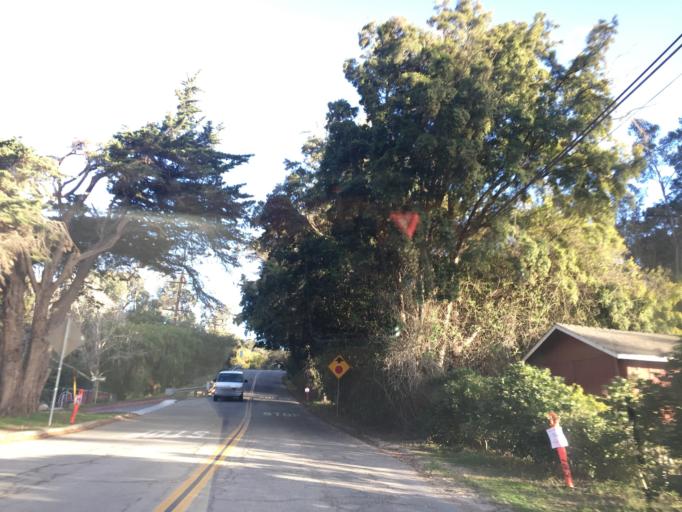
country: US
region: California
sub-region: Santa Barbara County
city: Goleta
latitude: 34.4356
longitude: -119.7706
